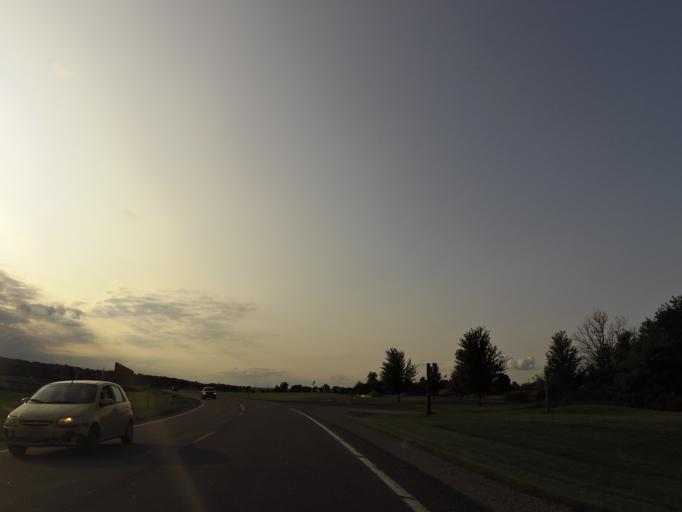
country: US
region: Minnesota
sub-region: Dakota County
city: Farmington
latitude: 44.6177
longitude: -93.0093
